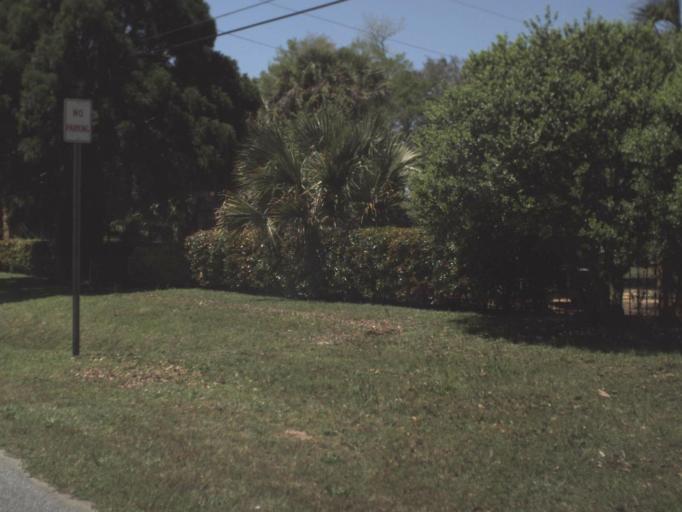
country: US
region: Florida
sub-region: Escambia County
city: Bellview
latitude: 30.4615
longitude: -87.3183
